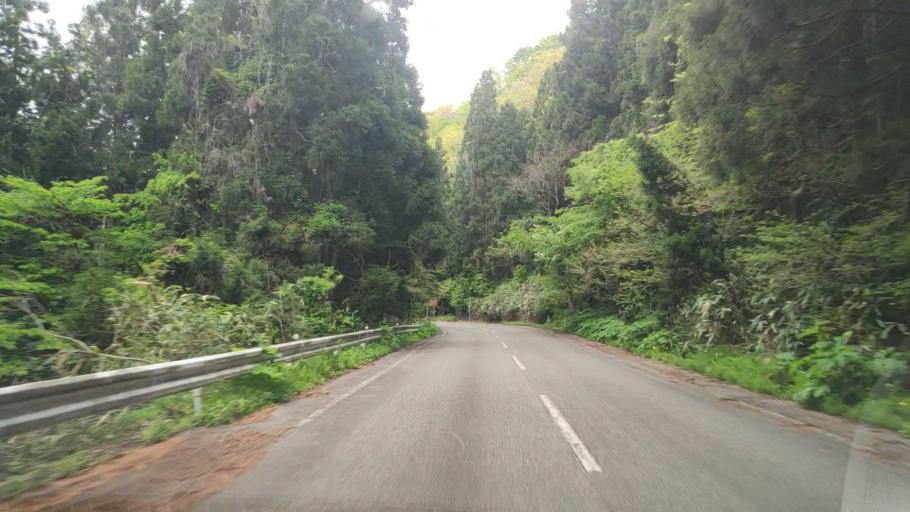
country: JP
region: Niigata
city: Gosen
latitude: 37.7099
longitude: 139.0954
